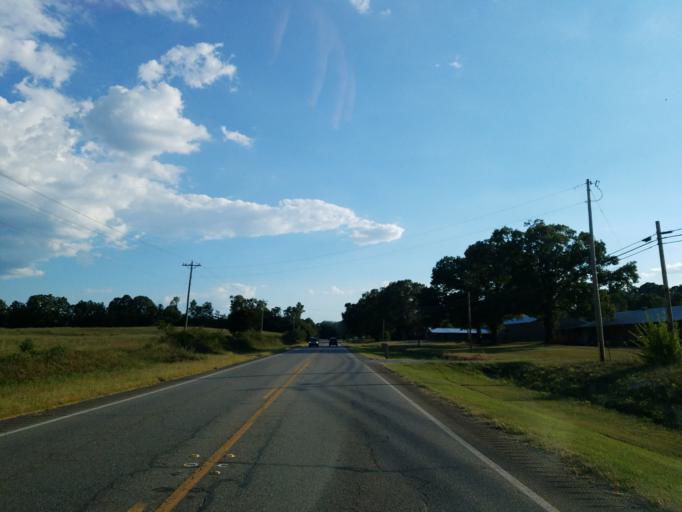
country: US
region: Georgia
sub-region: Murray County
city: Chatsworth
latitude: 34.8737
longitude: -84.7519
